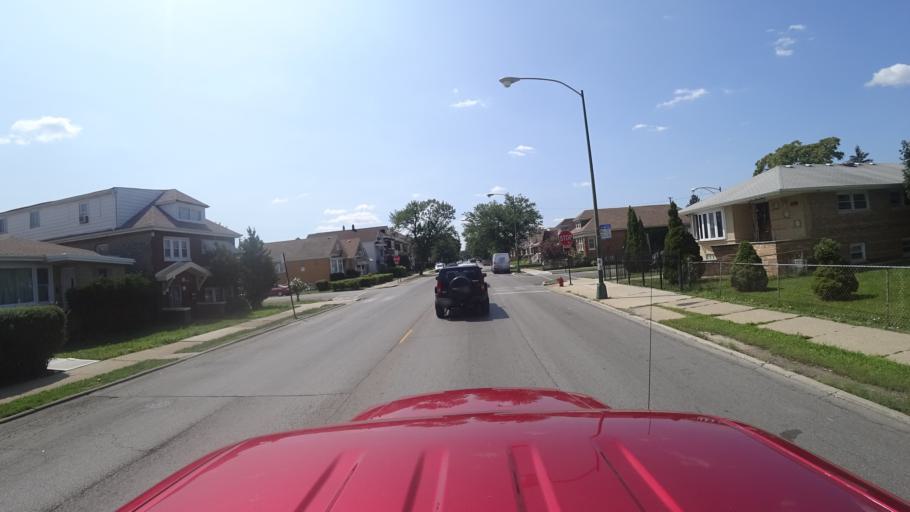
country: US
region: Illinois
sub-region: Cook County
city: Chicago
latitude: 41.7977
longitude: -87.6940
